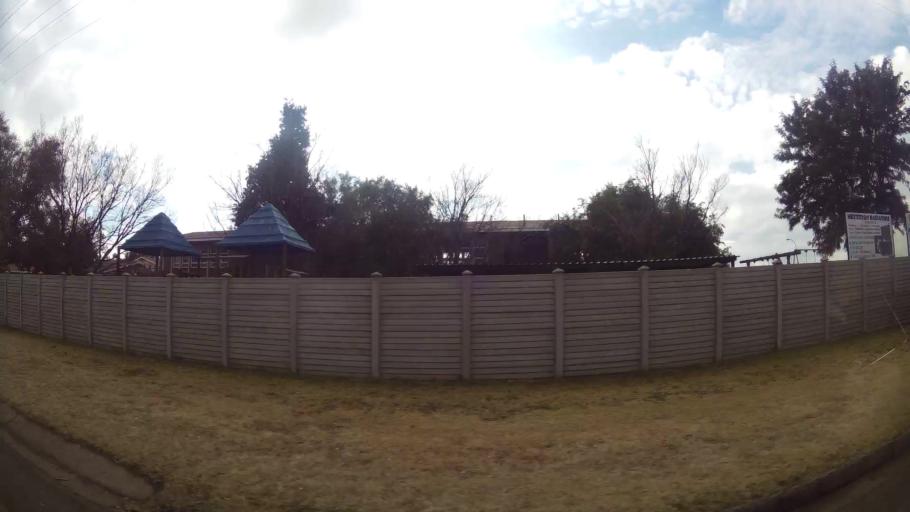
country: ZA
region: Gauteng
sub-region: Sedibeng District Municipality
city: Meyerton
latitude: -26.6025
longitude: 28.0467
